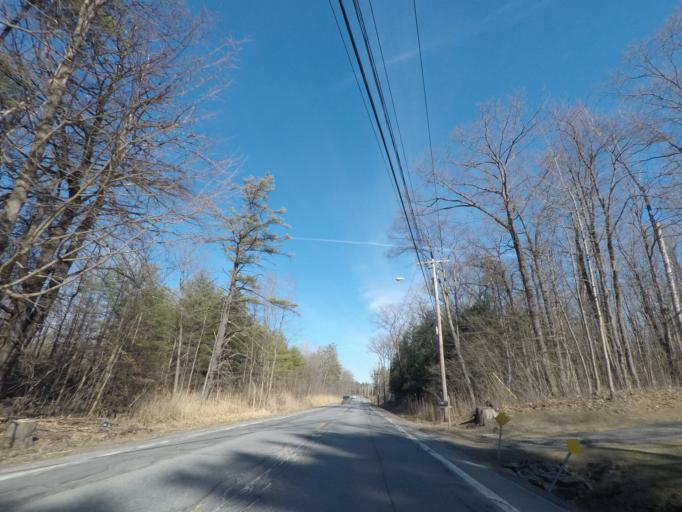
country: US
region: New York
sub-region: Saratoga County
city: Milton
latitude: 43.0755
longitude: -73.8437
